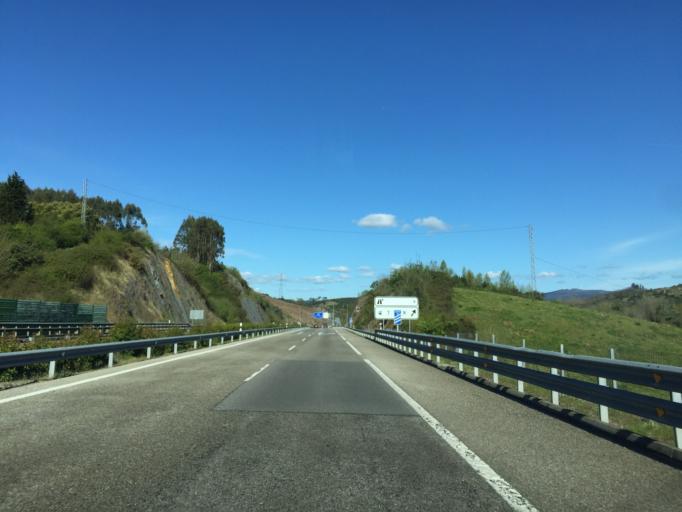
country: ES
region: Asturias
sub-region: Province of Asturias
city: Castandiello
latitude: 43.3578
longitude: -5.9419
